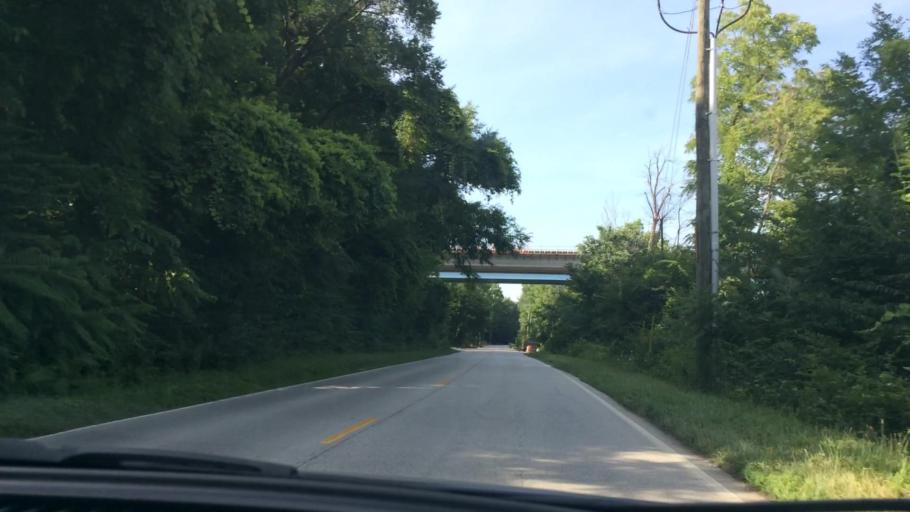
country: US
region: Indiana
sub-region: Tippecanoe County
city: West Lafayette
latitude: 40.4505
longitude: -86.8954
